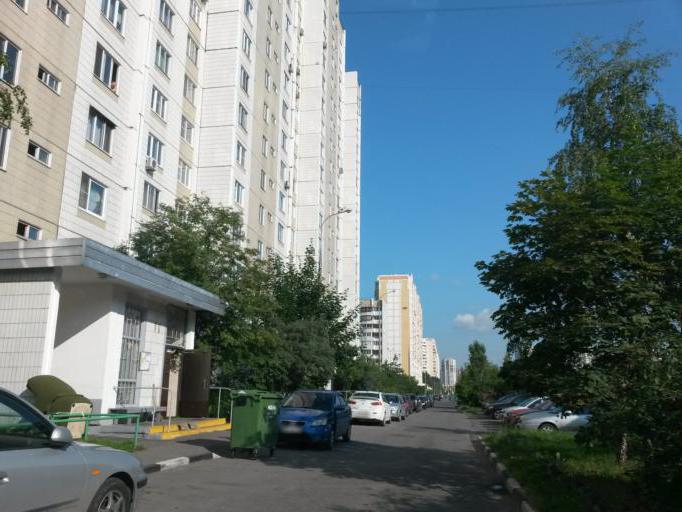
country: RU
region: Moscow
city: Brateyevo
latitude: 55.6572
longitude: 37.7690
